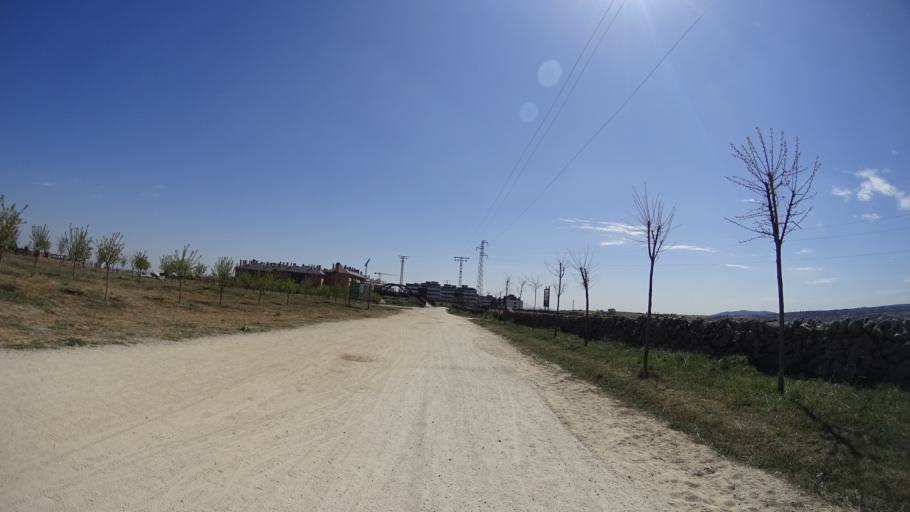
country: ES
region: Madrid
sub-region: Provincia de Madrid
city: Colmenar Viejo
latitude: 40.6542
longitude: -3.7902
